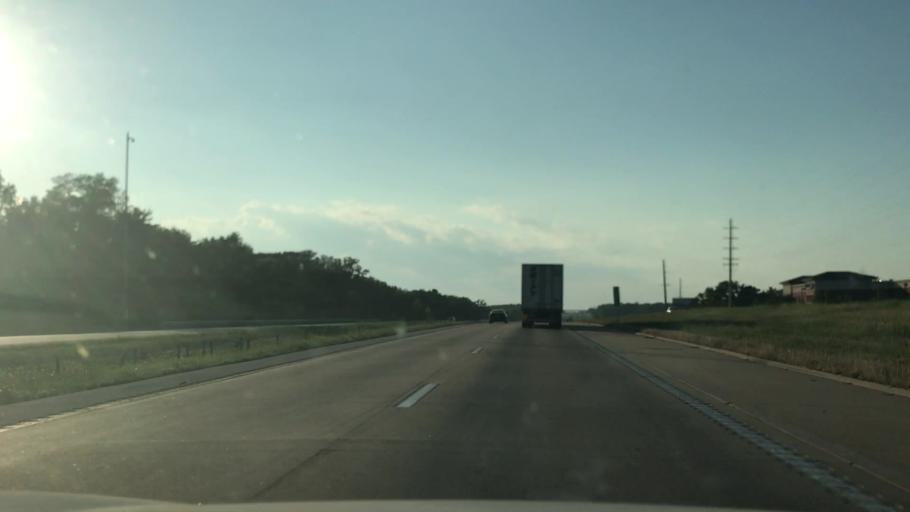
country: US
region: Missouri
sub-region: Saint Charles County
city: Dardenne Prairie
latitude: 38.7298
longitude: -90.7351
